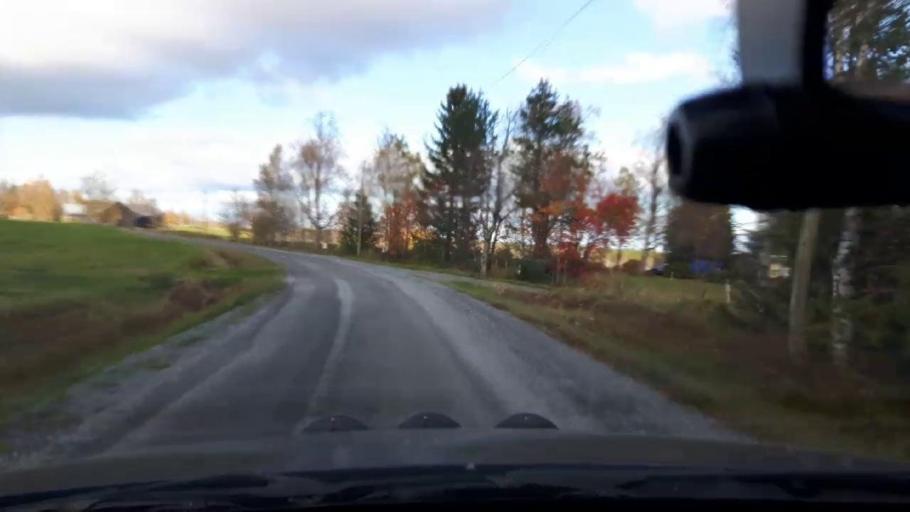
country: SE
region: Jaemtland
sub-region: Bergs Kommun
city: Hoverberg
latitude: 63.0559
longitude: 14.2394
